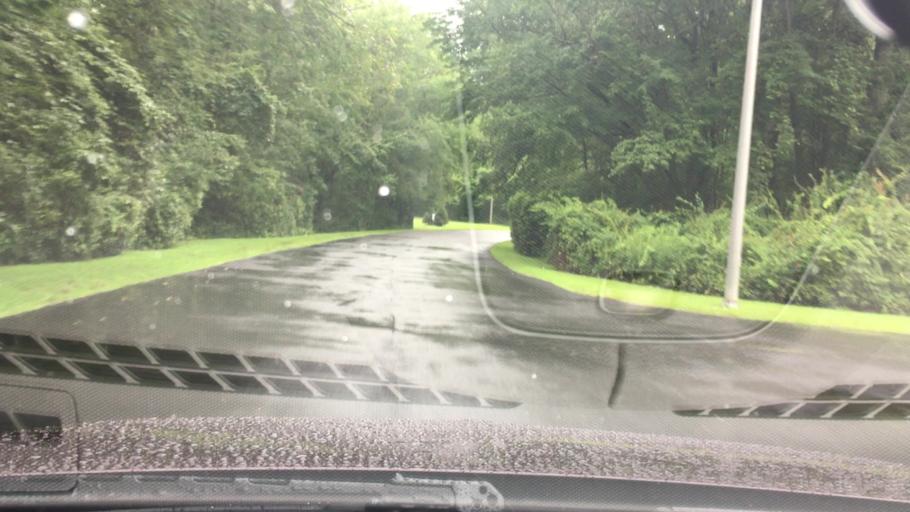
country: US
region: Connecticut
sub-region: New Haven County
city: Cheshire Village
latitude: 41.5560
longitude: -72.9127
